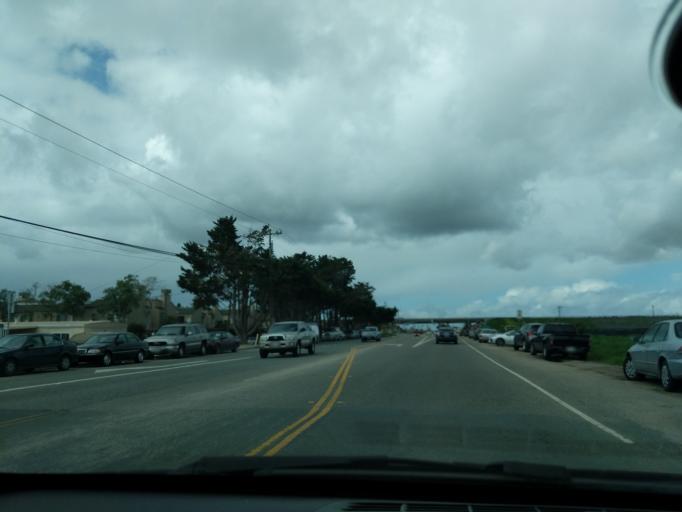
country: US
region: California
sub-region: Monterey County
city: Boronda
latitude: 36.7335
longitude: -121.6530
